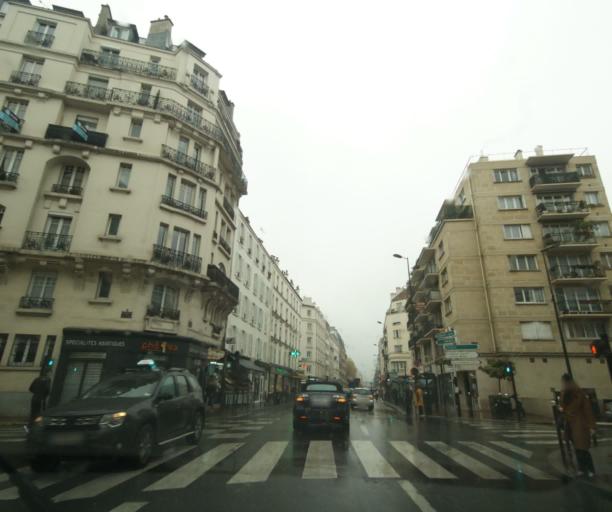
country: FR
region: Ile-de-France
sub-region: Departement des Hauts-de-Seine
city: Levallois-Perret
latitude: 48.8954
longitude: 2.2970
